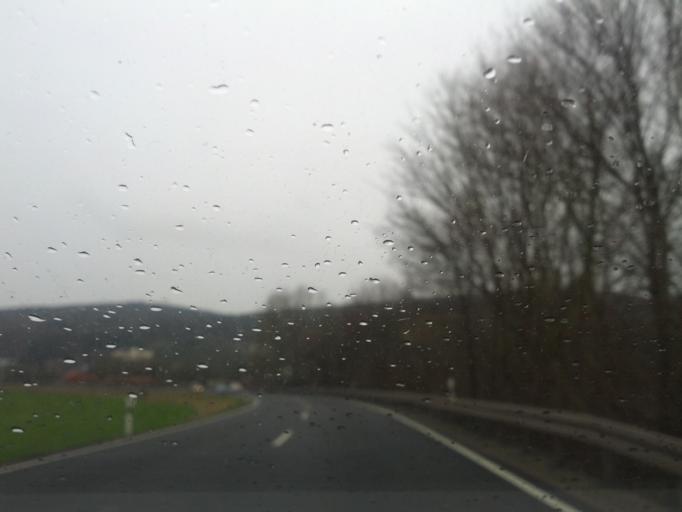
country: DE
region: Hesse
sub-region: Regierungsbezirk Kassel
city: Bad Sooden-Allendorf
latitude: 51.2828
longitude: 9.9647
